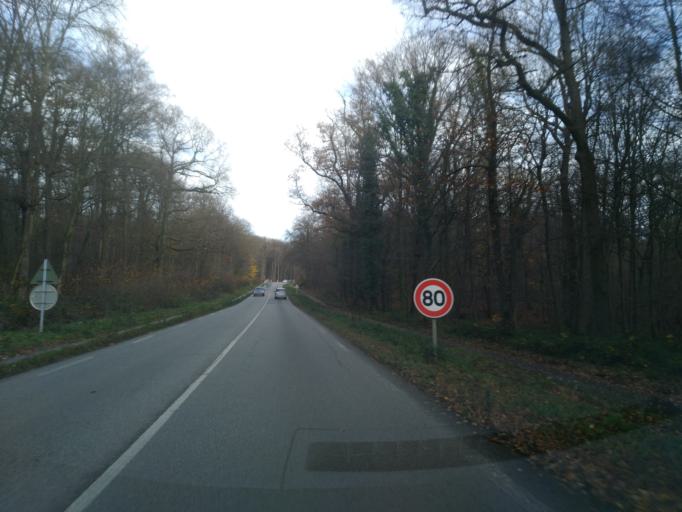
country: FR
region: Ile-de-France
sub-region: Departement des Yvelines
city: Saint-Nom-la-Breteche
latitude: 48.8691
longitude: 2.0381
